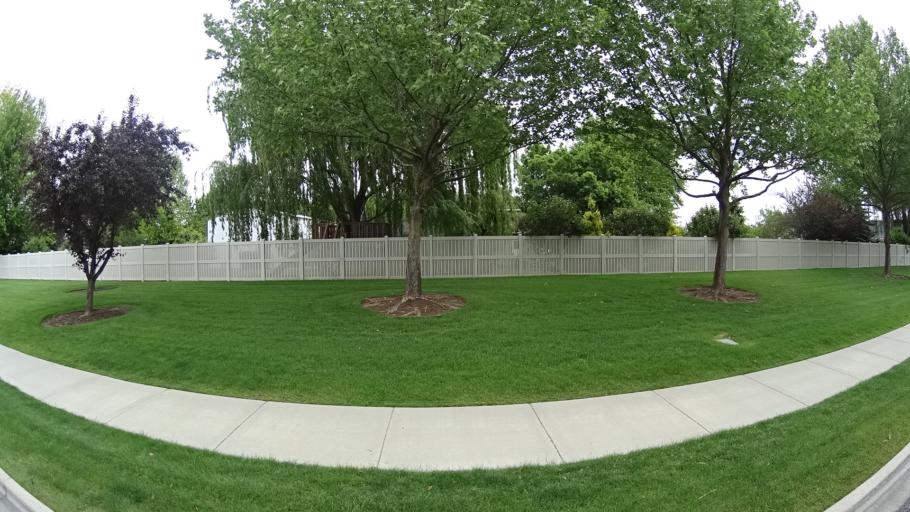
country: US
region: Idaho
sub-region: Ada County
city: Meridian
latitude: 43.6379
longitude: -116.4246
